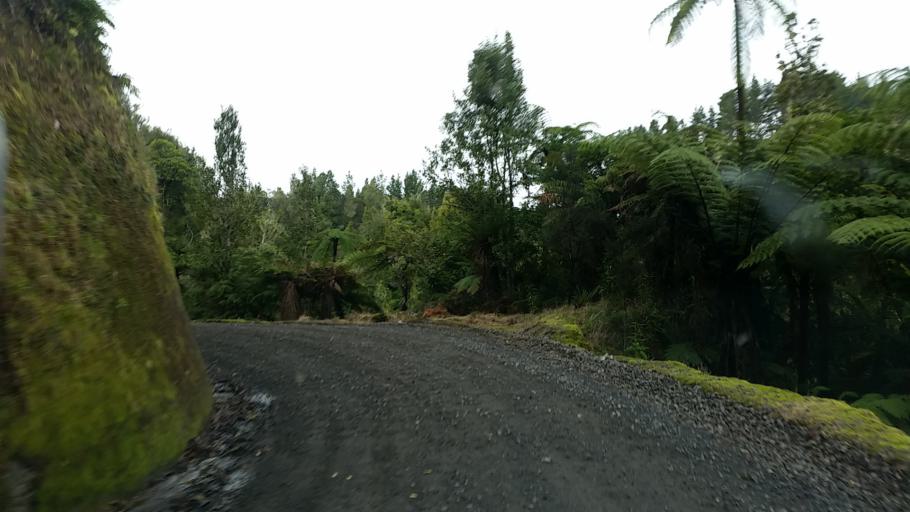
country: NZ
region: Taranaki
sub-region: New Plymouth District
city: Waitara
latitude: -39.1621
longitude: 174.5485
